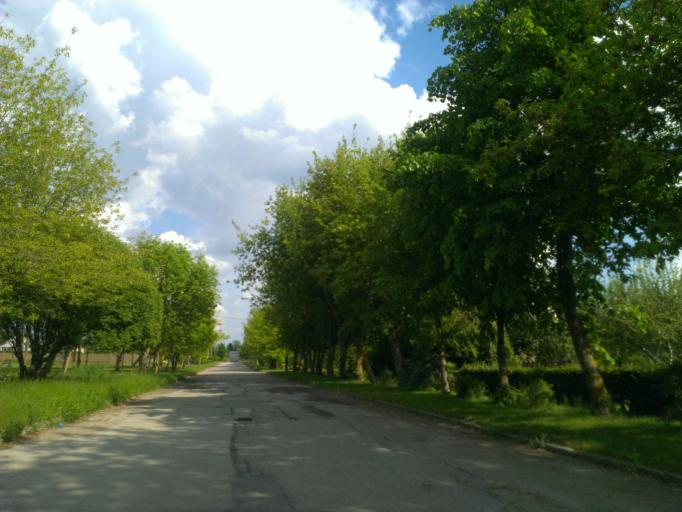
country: LT
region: Klaipedos apskritis
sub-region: Klaipeda
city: Palanga
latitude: 55.9062
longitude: 21.1299
